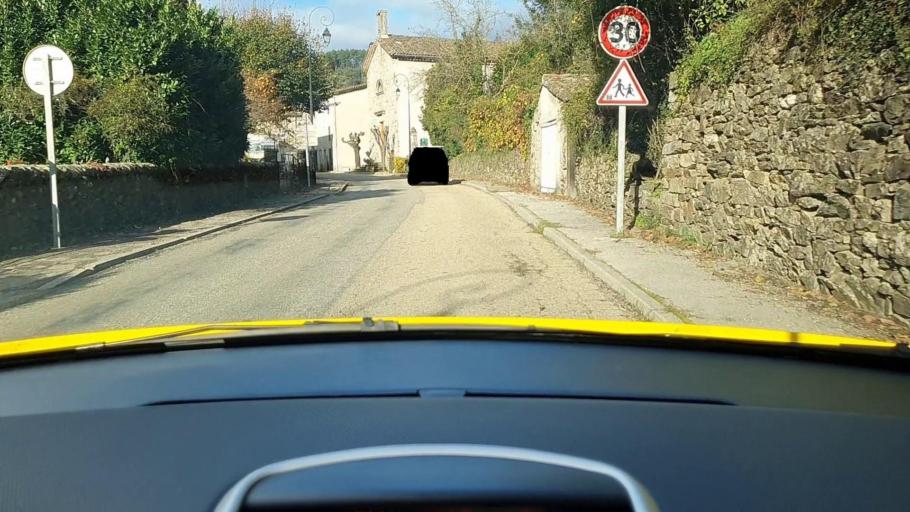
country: FR
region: Languedoc-Roussillon
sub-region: Departement du Gard
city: Lasalle
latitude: 44.1071
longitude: 3.7849
